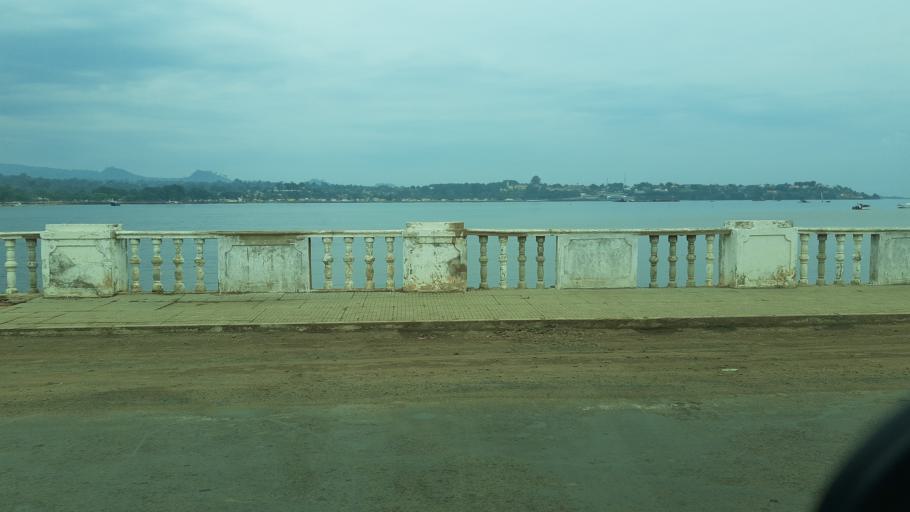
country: ST
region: Sao Tome Island
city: Sao Tome
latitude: 0.3419
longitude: 6.7354
